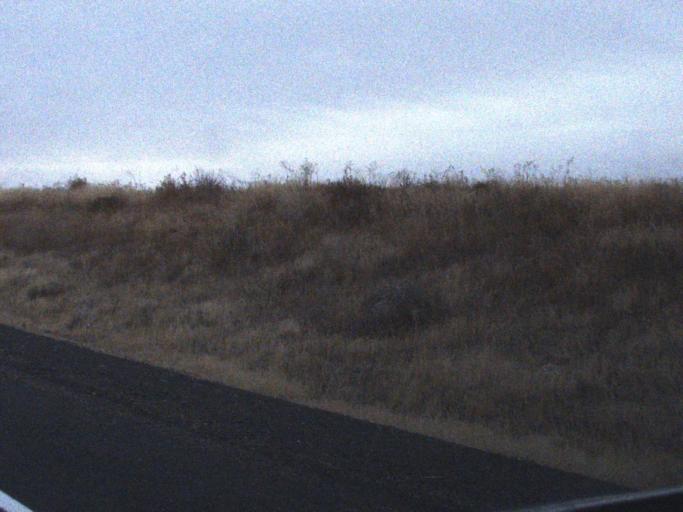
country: US
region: Washington
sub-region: Franklin County
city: Connell
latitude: 46.7944
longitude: -118.7094
